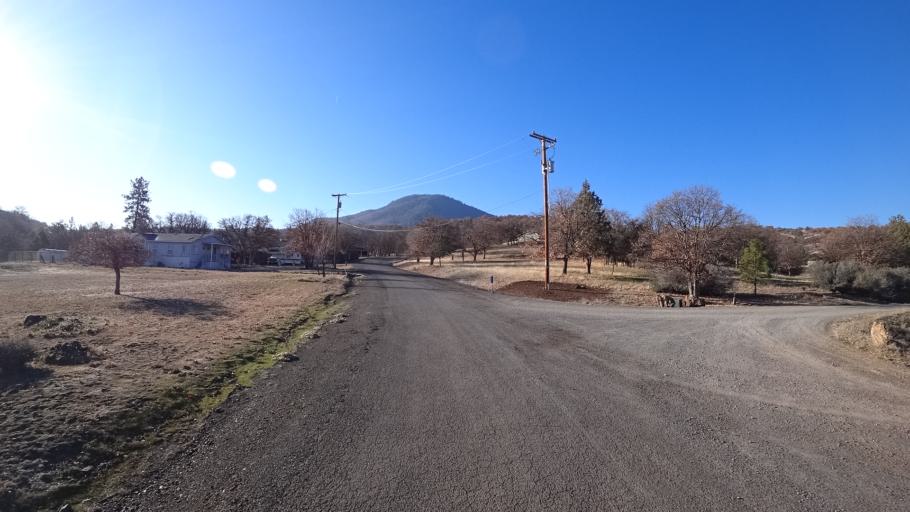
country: US
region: California
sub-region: Siskiyou County
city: Montague
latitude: 41.8956
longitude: -122.5019
